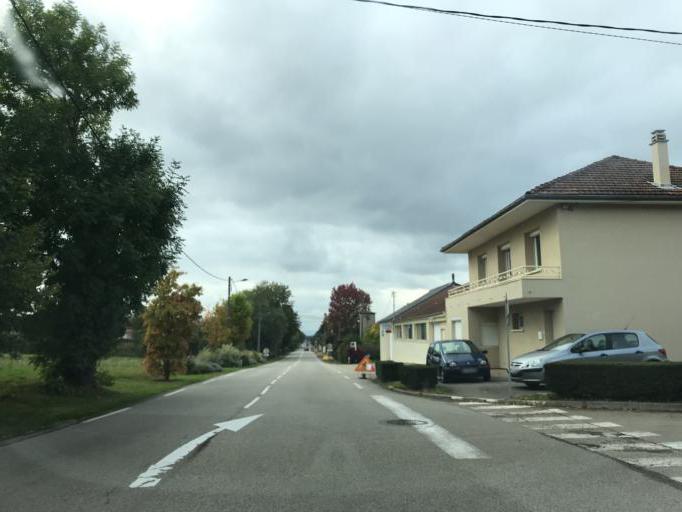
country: FR
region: Rhone-Alpes
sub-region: Departement de l'Ain
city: Jasseron
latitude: 46.2118
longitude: 5.3213
